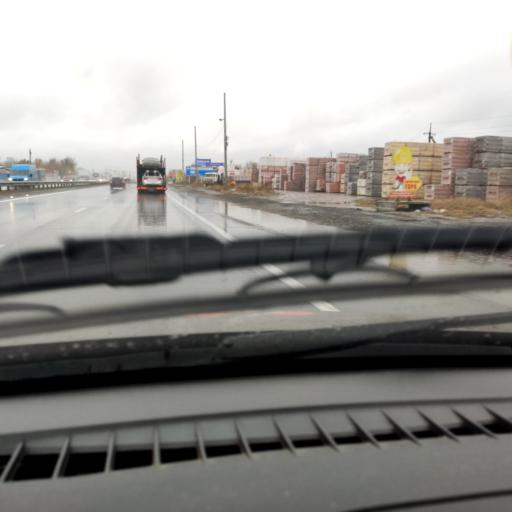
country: RU
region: Samara
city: Tol'yatti
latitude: 53.5622
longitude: 49.3624
